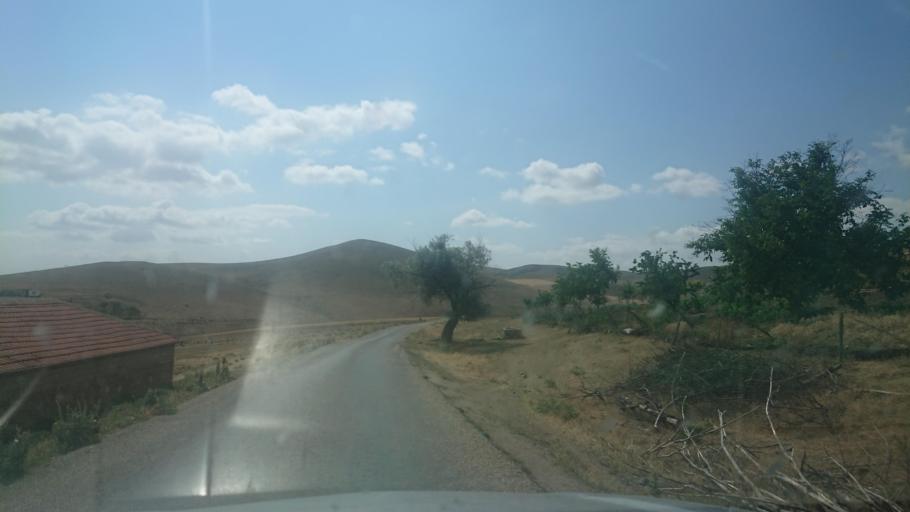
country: TR
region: Aksaray
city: Sariyahsi
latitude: 39.0114
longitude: 33.9463
